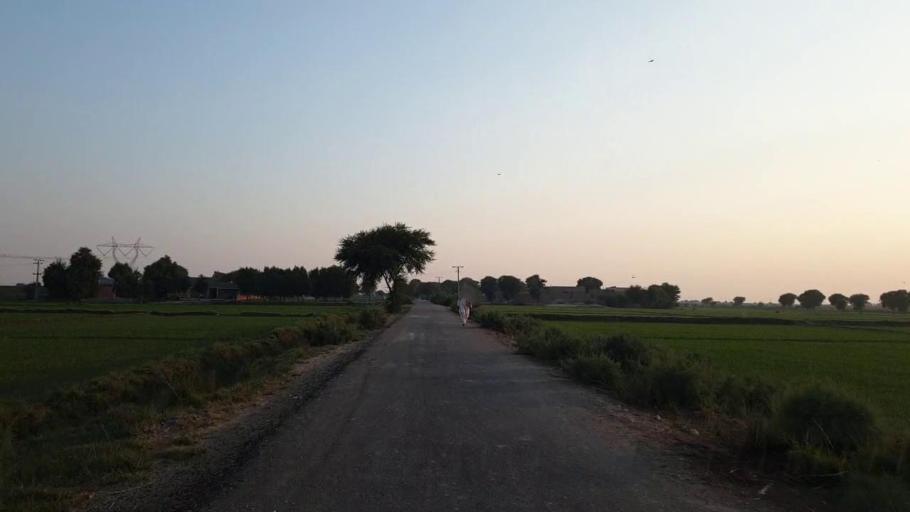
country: PK
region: Sindh
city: Sehwan
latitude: 26.4452
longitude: 67.7618
